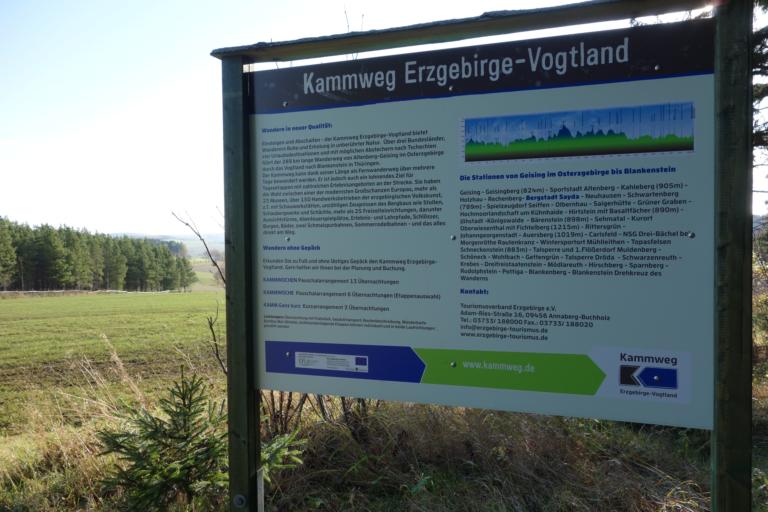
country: DE
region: Saxony
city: Neuhausen
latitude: 50.7095
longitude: 13.4644
